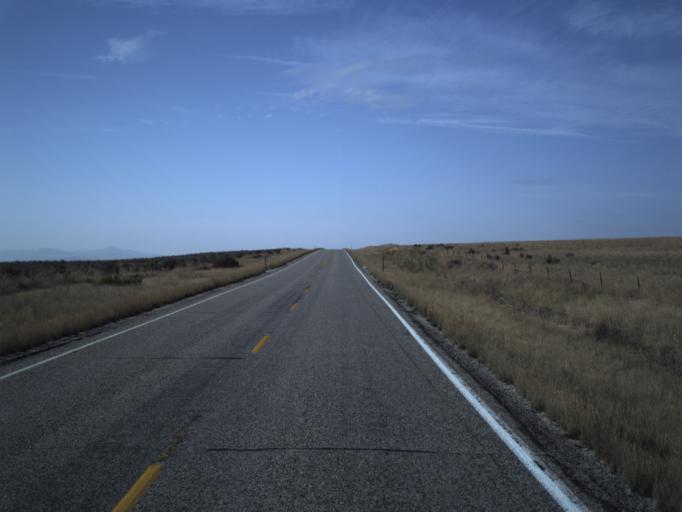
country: US
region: Idaho
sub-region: Oneida County
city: Malad City
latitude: 41.9455
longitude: -113.0814
